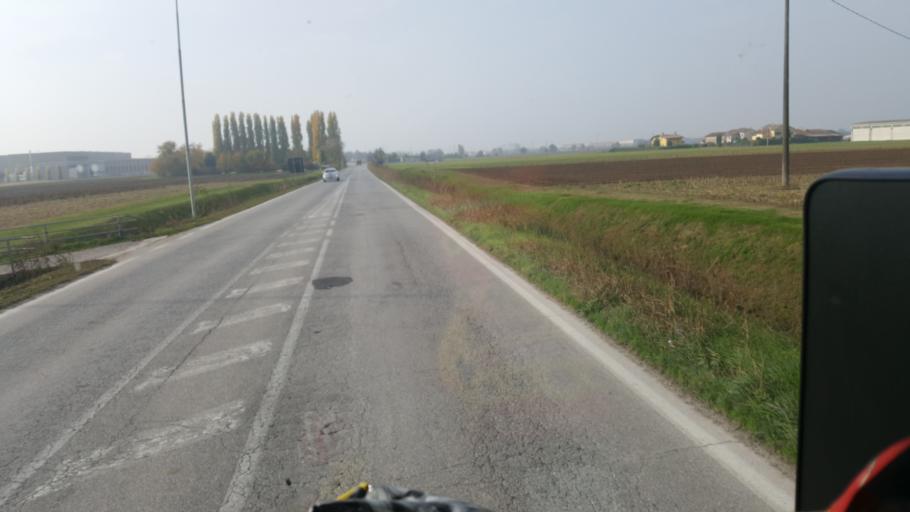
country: IT
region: Lombardy
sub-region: Provincia di Mantova
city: Gazoldo degli Ippoliti
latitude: 45.2117
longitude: 10.6010
